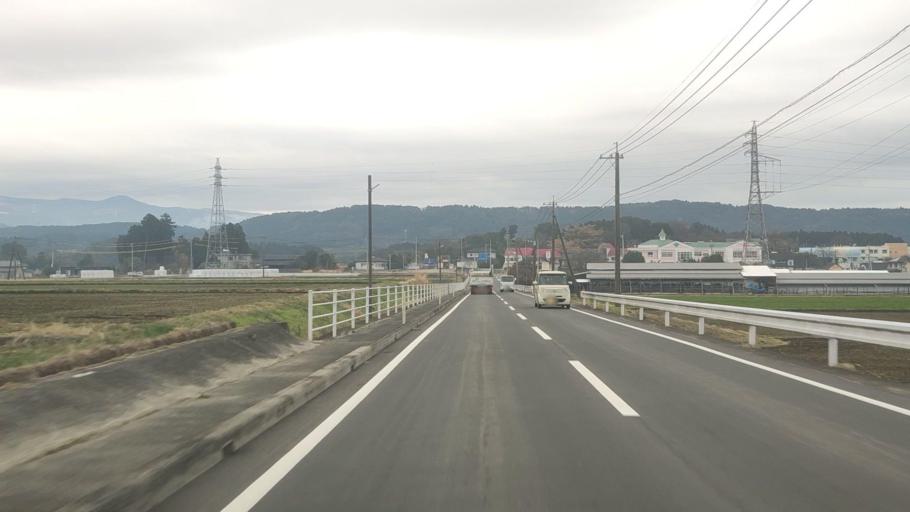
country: JP
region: Kumamoto
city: Ozu
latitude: 32.8676
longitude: 130.8904
